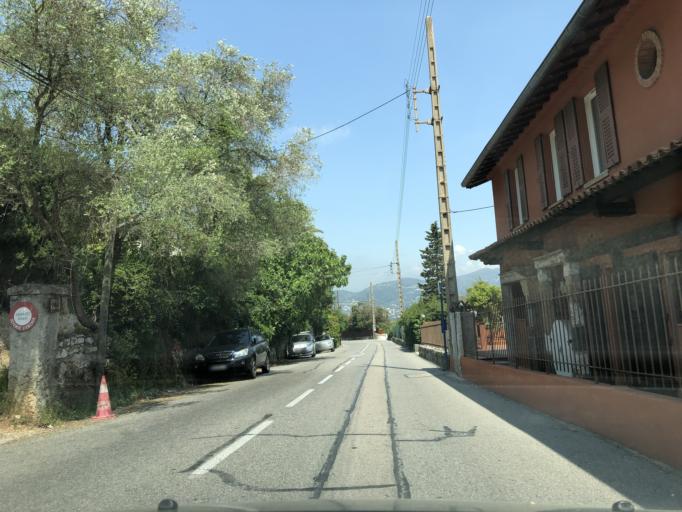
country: FR
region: Provence-Alpes-Cote d'Azur
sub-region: Departement des Alpes-Maritimes
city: Villefranche-sur-Mer
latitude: 43.7178
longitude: 7.3104
